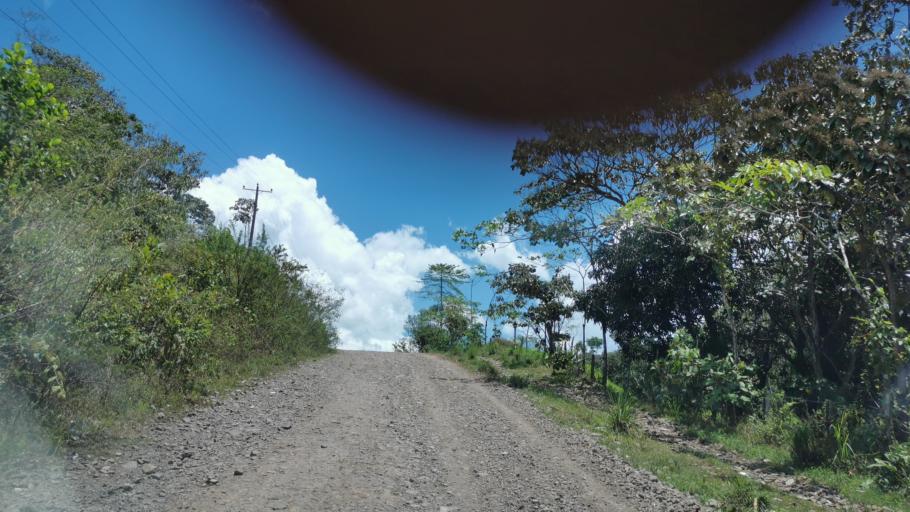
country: NI
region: Atlantico Sur
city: Rama
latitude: 12.3902
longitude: -84.3119
